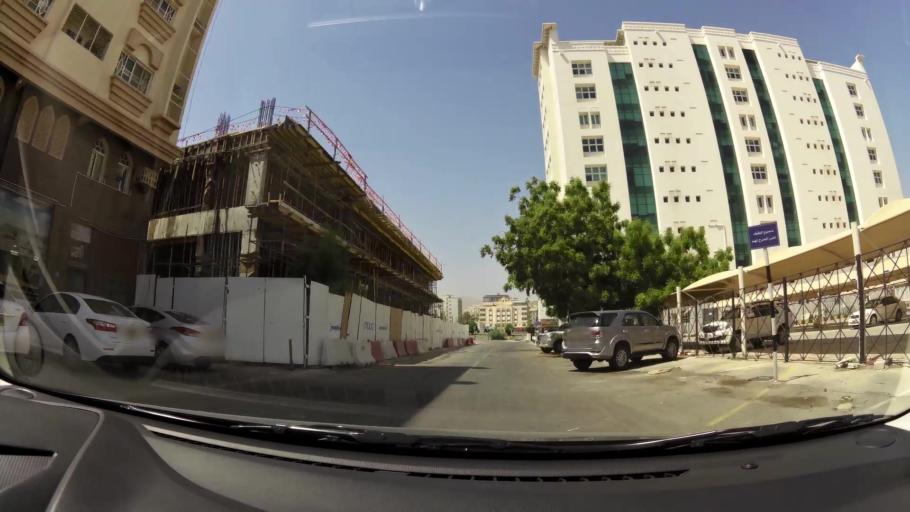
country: OM
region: Muhafazat Masqat
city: Bawshar
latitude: 23.5846
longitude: 58.3970
